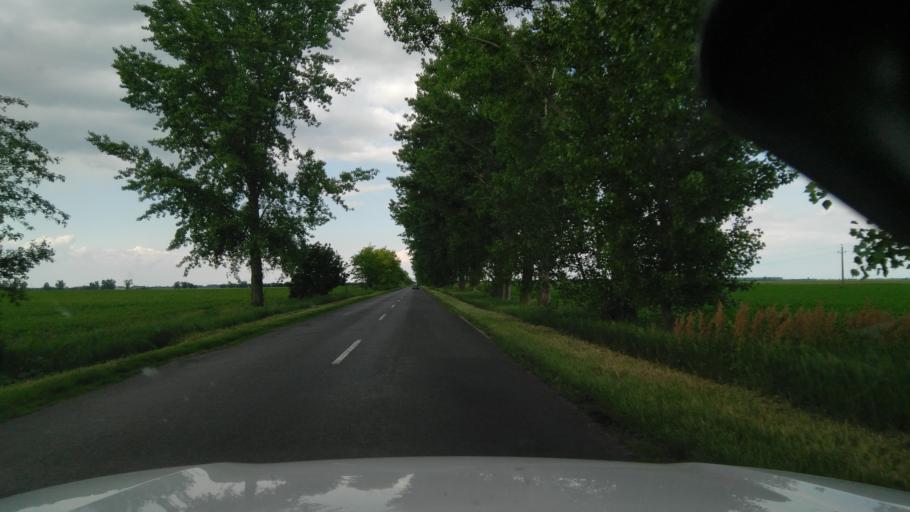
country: HU
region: Bekes
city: Magyarbanhegyes
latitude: 46.4550
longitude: 20.9995
